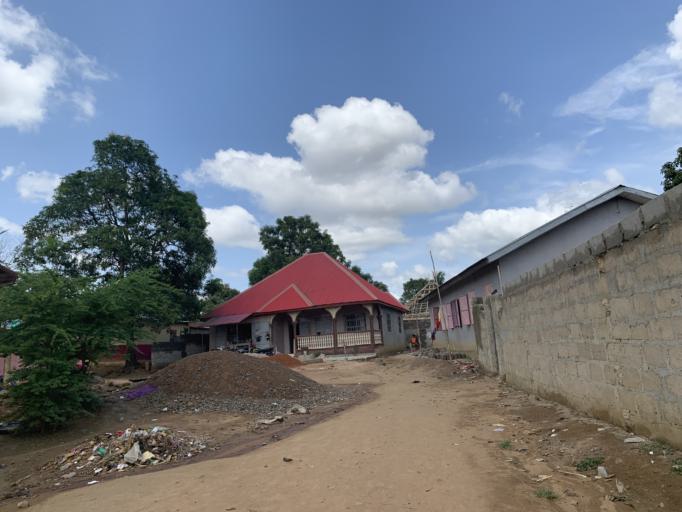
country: SL
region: Western Area
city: Waterloo
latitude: 8.3355
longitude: -13.0443
